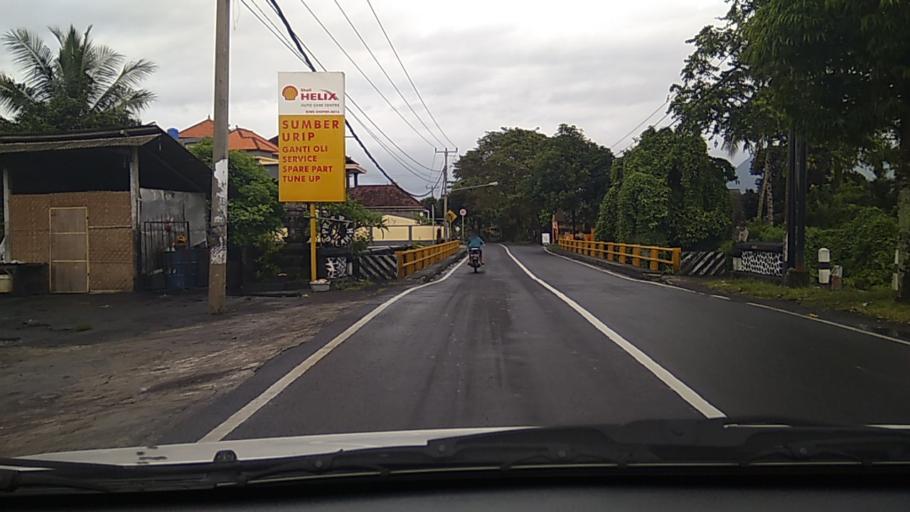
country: ID
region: Bali
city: Banjar Budakeling
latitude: -8.4335
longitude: 115.5905
